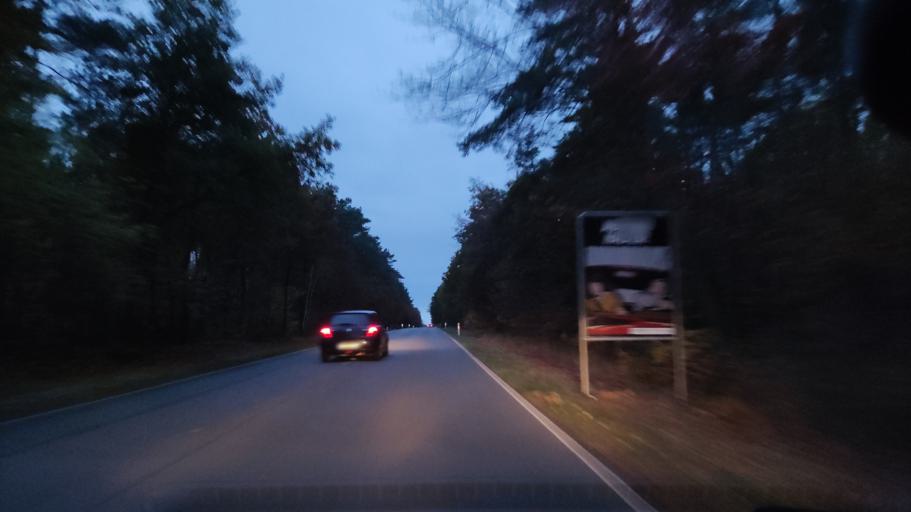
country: DE
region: Lower Saxony
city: Munster
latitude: 53.0163
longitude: 10.0784
